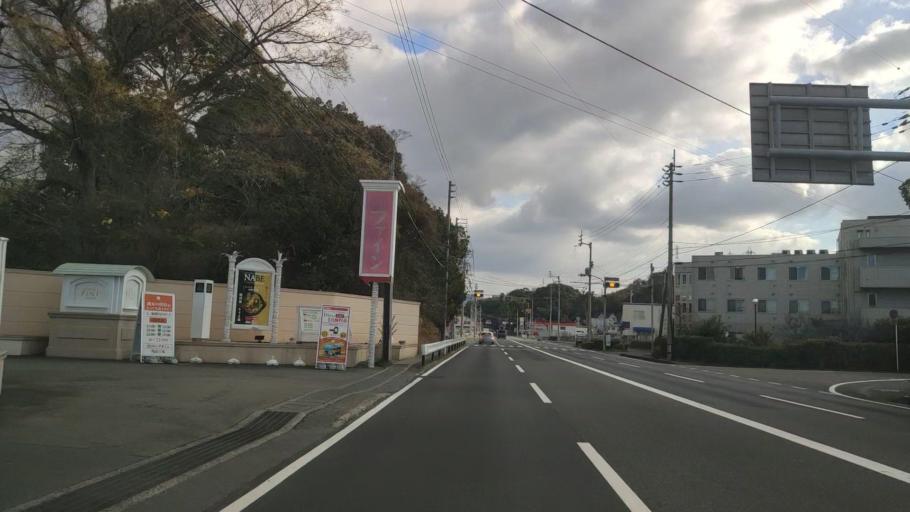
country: JP
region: Ehime
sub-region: Shikoku-chuo Shi
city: Matsuyama
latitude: 33.8566
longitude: 132.7291
